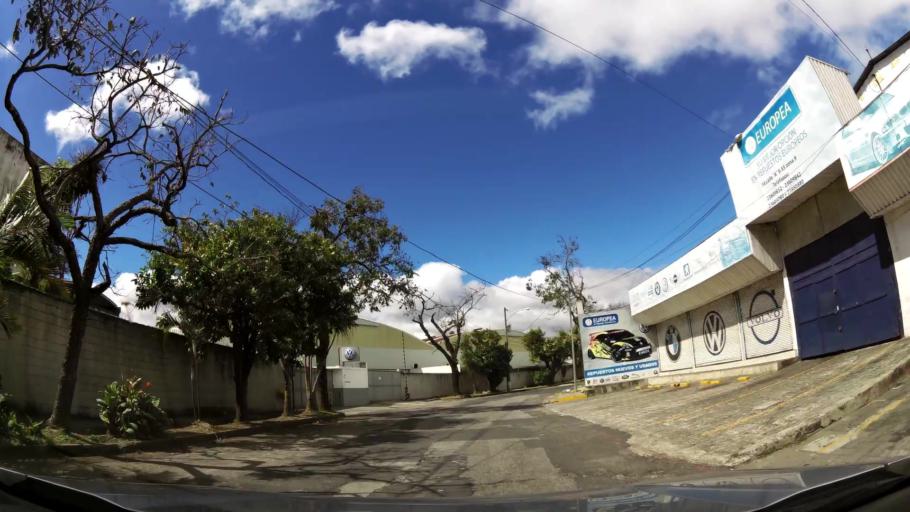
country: GT
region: Guatemala
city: Santa Catarina Pinula
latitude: 14.5970
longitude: -90.5231
